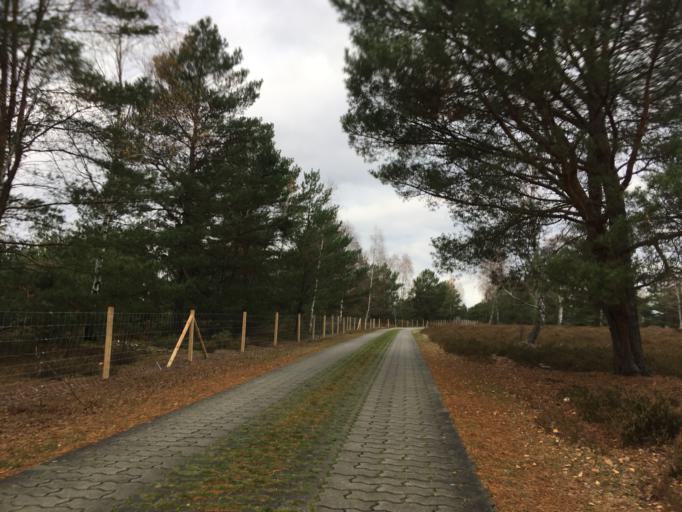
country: DE
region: Brandenburg
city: Tauer
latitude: 52.0070
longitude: 14.4986
